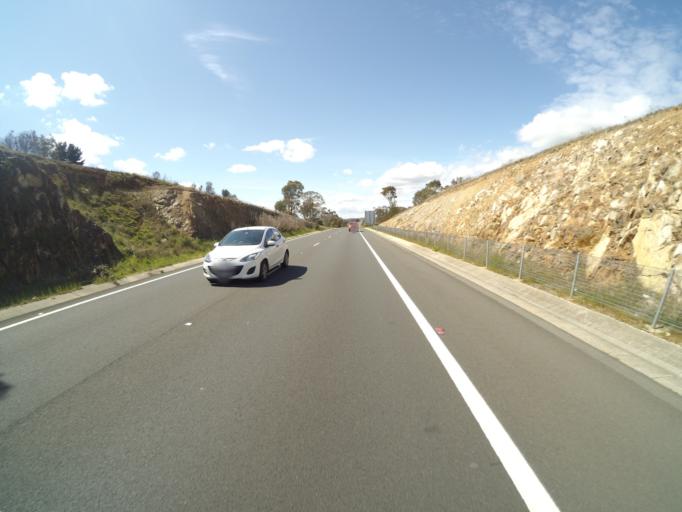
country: AU
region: New South Wales
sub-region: Goulburn Mulwaree
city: Goulburn
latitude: -34.7383
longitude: 149.7820
